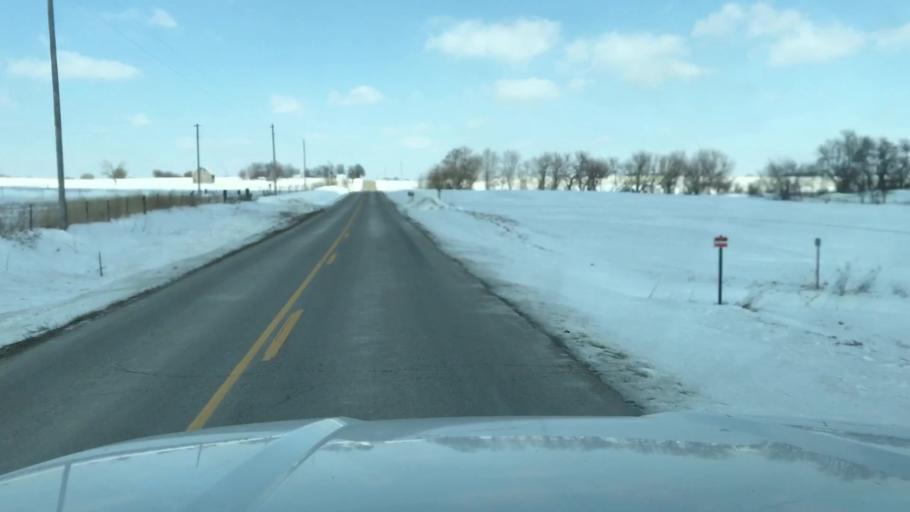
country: US
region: Missouri
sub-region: Nodaway County
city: Maryville
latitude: 40.3490
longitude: -94.7224
